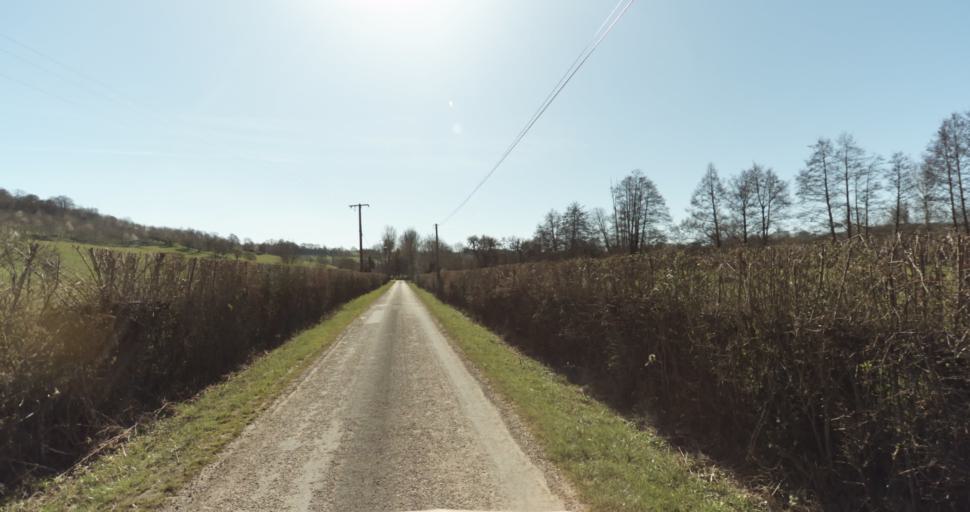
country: FR
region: Lower Normandy
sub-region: Departement du Calvados
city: Livarot
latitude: 48.9596
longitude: 0.0694
